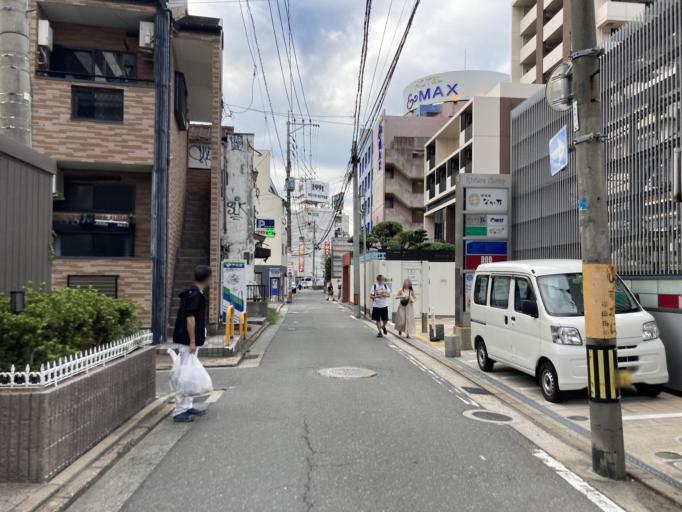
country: JP
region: Fukuoka
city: Fukuoka-shi
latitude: 33.5878
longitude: 130.4087
